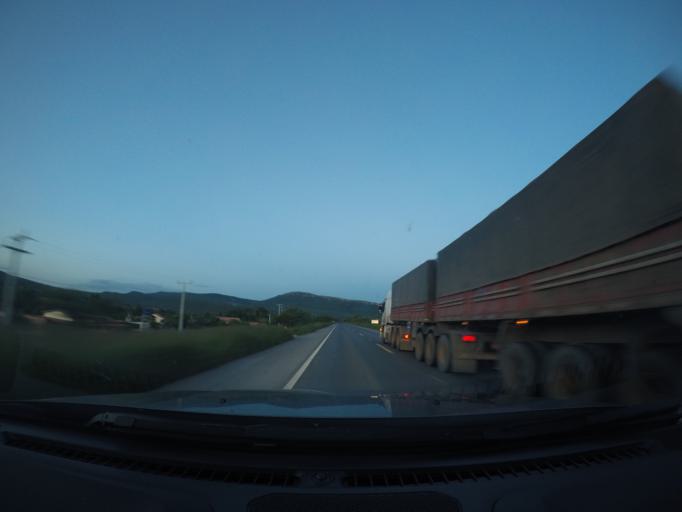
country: BR
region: Bahia
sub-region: Seabra
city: Seabra
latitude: -12.4801
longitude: -41.7187
